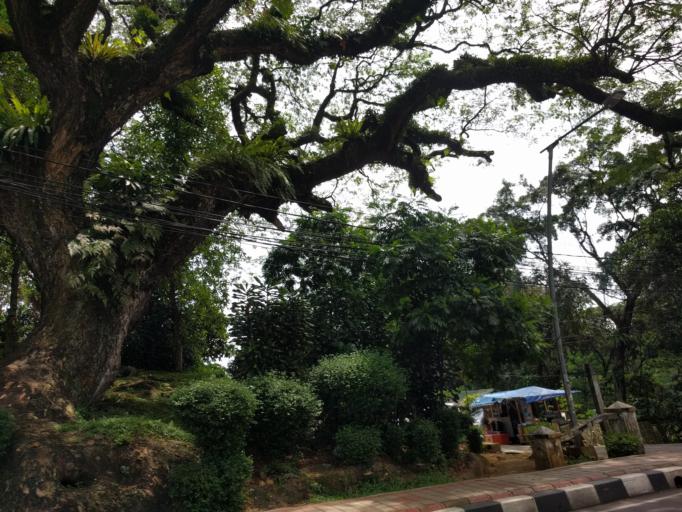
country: ID
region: West Java
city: Bogor
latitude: -6.5935
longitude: 106.7983
